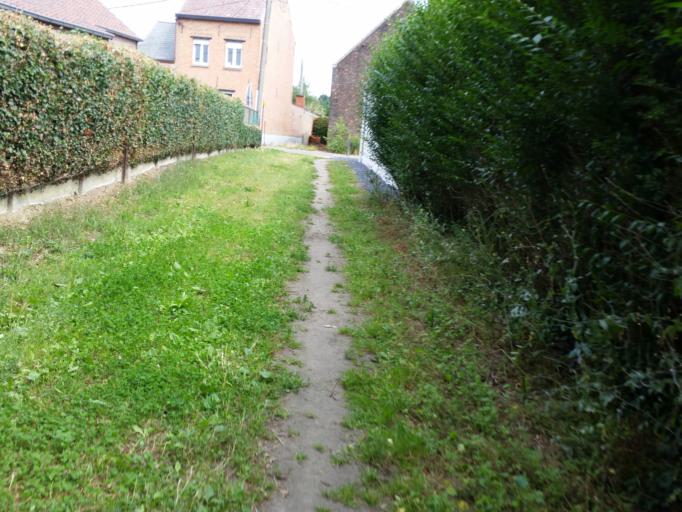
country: BE
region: Flanders
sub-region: Provincie Vlaams-Brabant
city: Zemst
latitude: 50.9705
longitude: 4.4679
